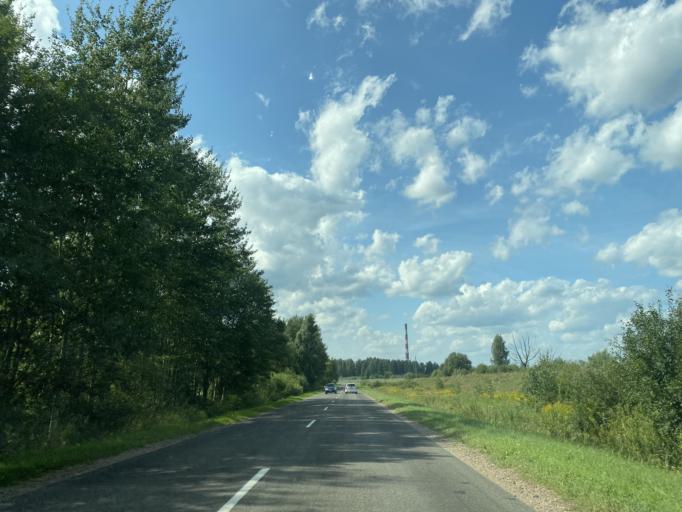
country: BY
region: Minsk
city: Horad Zhodzina
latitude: 54.0849
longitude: 28.3727
